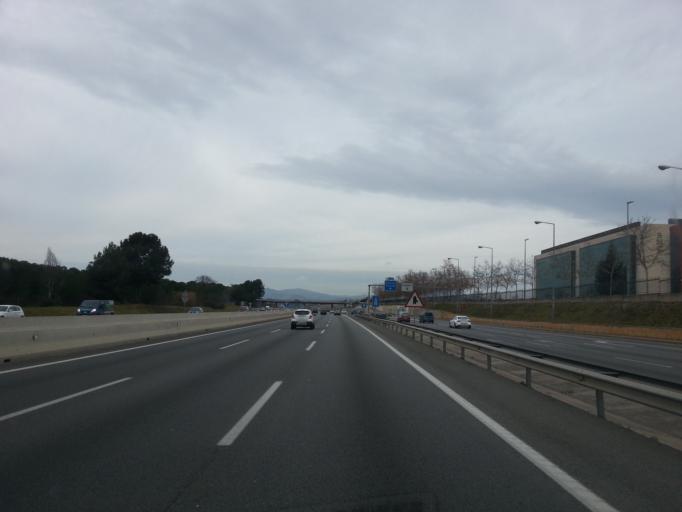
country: ES
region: Catalonia
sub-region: Provincia de Barcelona
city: Sant Quirze del Valles
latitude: 41.5353
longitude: 2.0890
